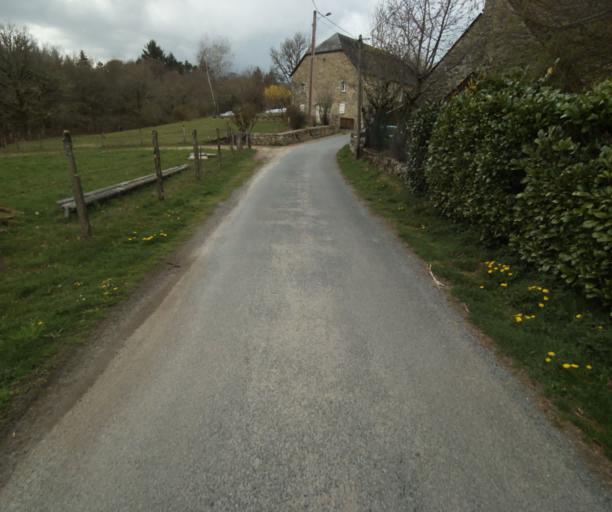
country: FR
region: Limousin
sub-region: Departement de la Correze
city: Correze
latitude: 45.2698
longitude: 1.9627
